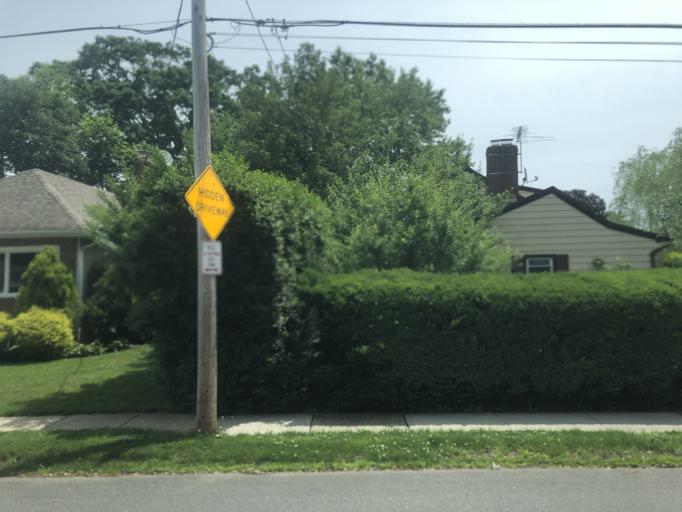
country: US
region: New York
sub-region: Nassau County
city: South Hempstead
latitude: 40.6830
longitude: -73.6268
